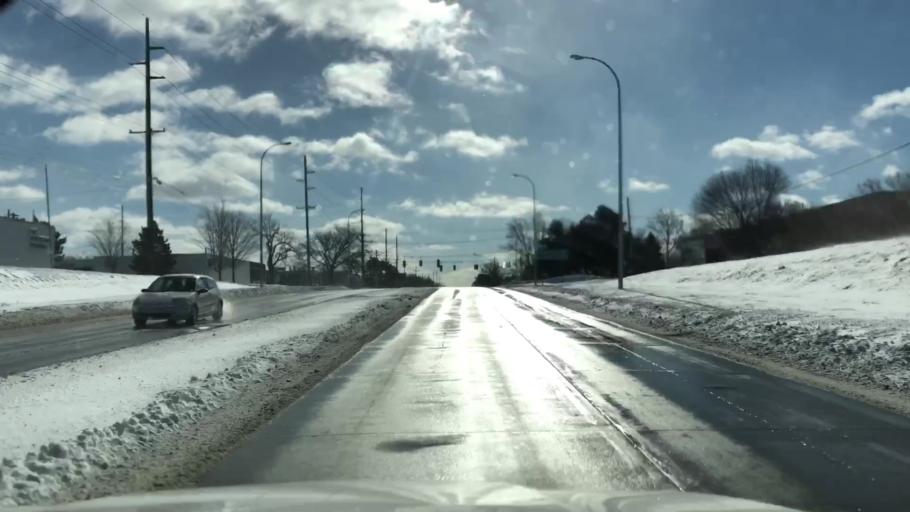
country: US
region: Michigan
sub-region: Wayne County
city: Westland
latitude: 42.3764
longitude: -83.4119
